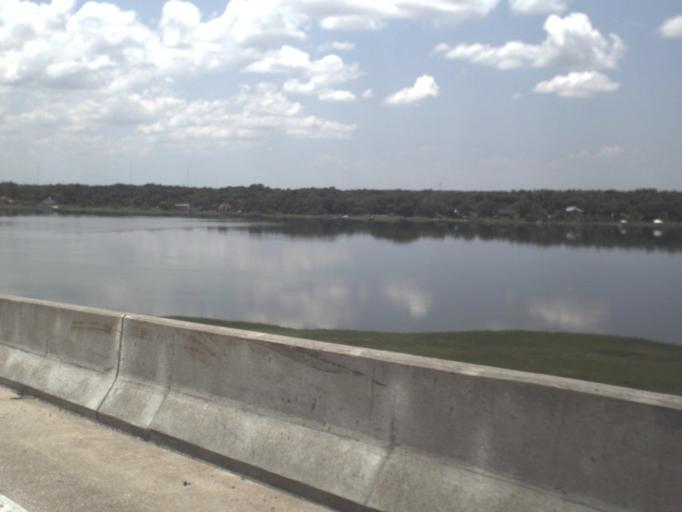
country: US
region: Florida
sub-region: Duval County
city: Jacksonville
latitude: 30.3785
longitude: -81.5545
